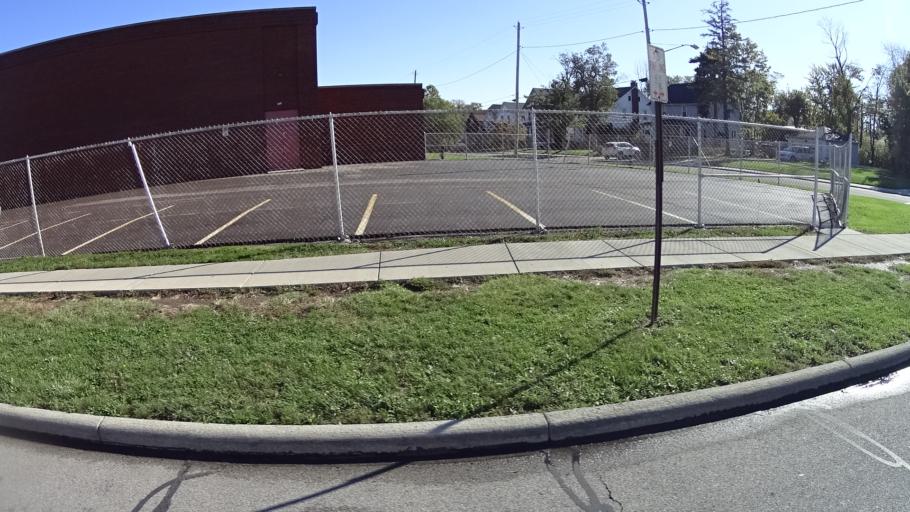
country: US
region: Ohio
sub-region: Lorain County
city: Lorain
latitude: 41.4659
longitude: -82.1849
